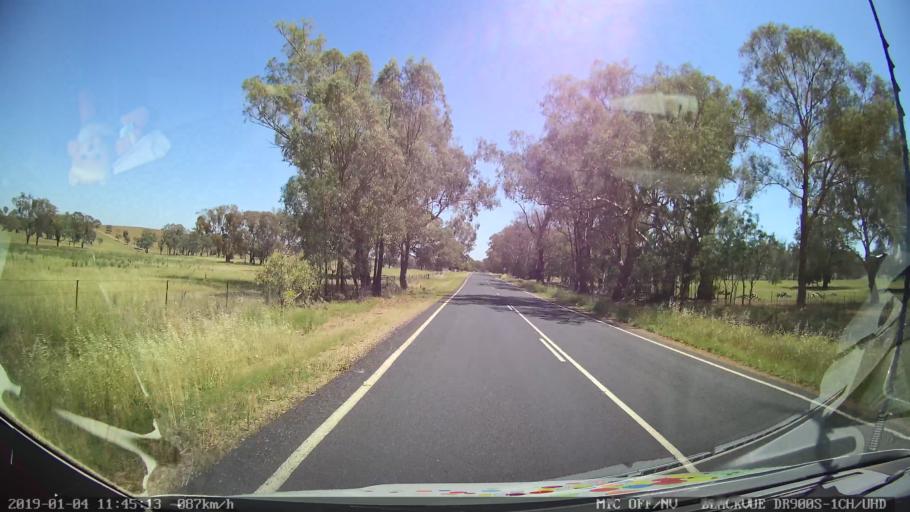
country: AU
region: New South Wales
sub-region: Cabonne
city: Molong
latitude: -32.9567
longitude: 148.7642
